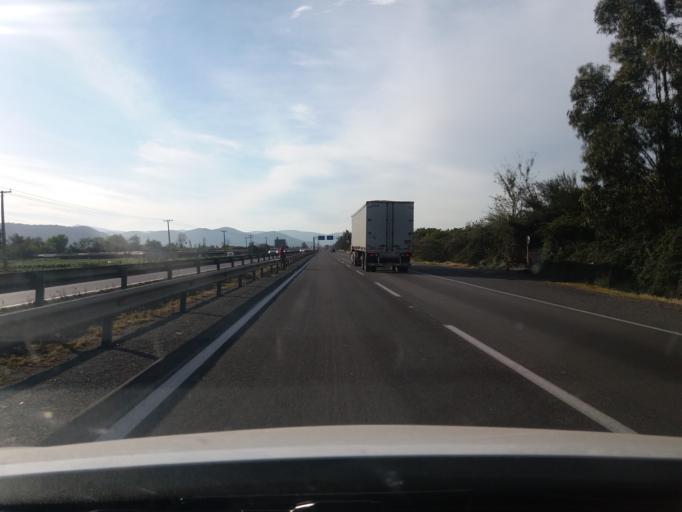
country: CL
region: Valparaiso
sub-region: Provincia de Quillota
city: Hacienda La Calera
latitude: -32.8201
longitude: -71.1395
